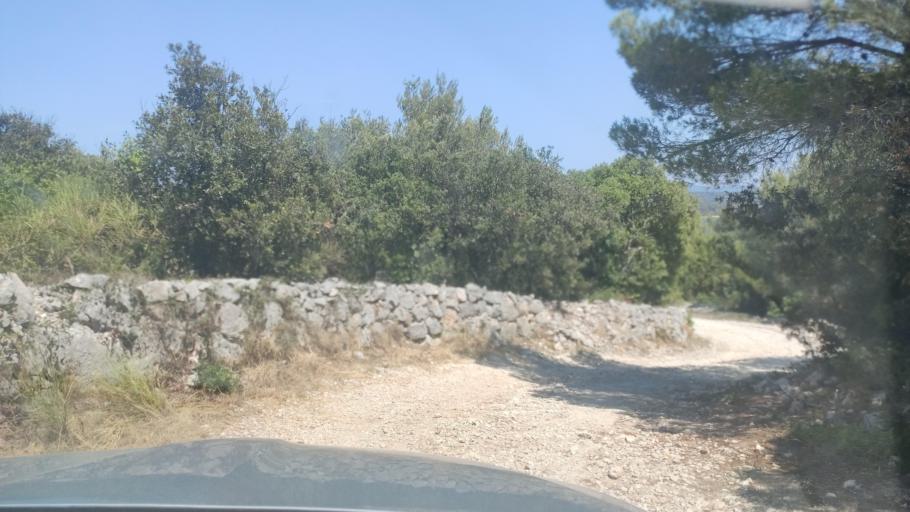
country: HR
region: Sibensko-Kniniska
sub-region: Grad Sibenik
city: Tisno
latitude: 43.7772
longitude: 15.6531
